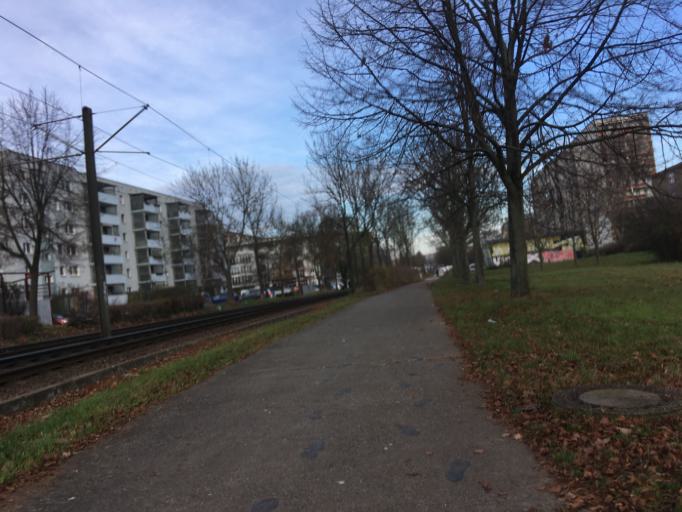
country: DE
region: Brandenburg
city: Ahrensfelde
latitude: 52.5629
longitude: 13.5702
